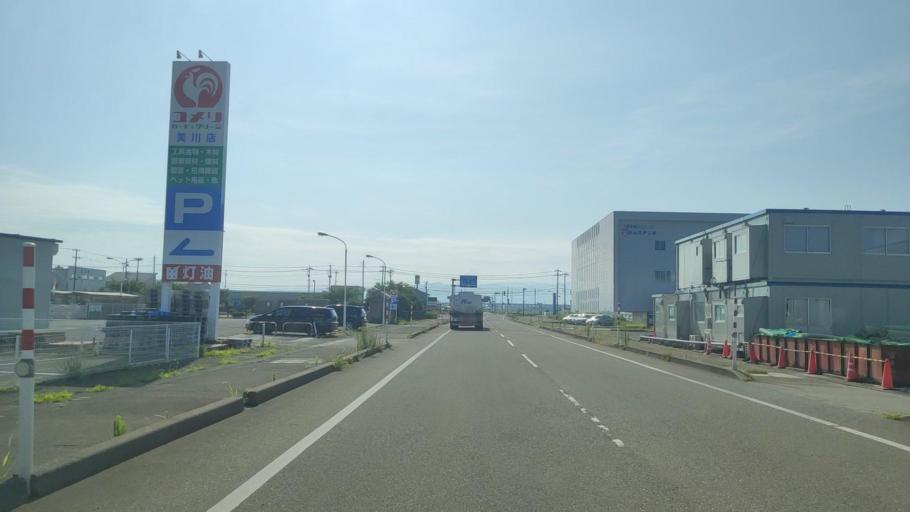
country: JP
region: Ishikawa
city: Matsuto
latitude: 36.5013
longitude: 136.5031
